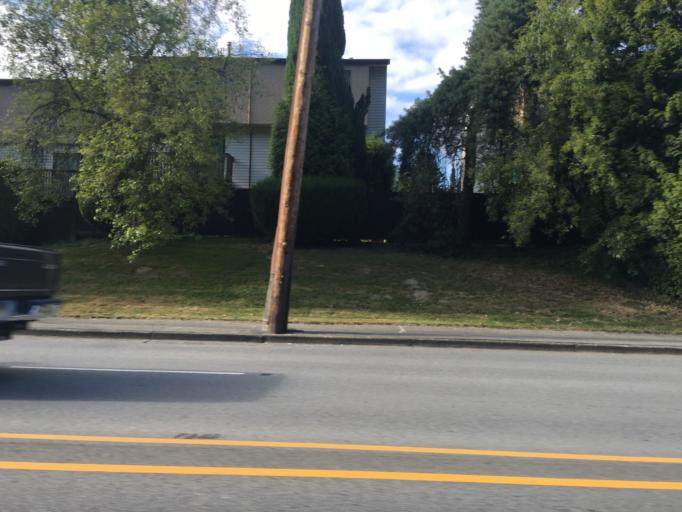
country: CA
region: British Columbia
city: Port Moody
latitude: 49.2489
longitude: -122.8573
